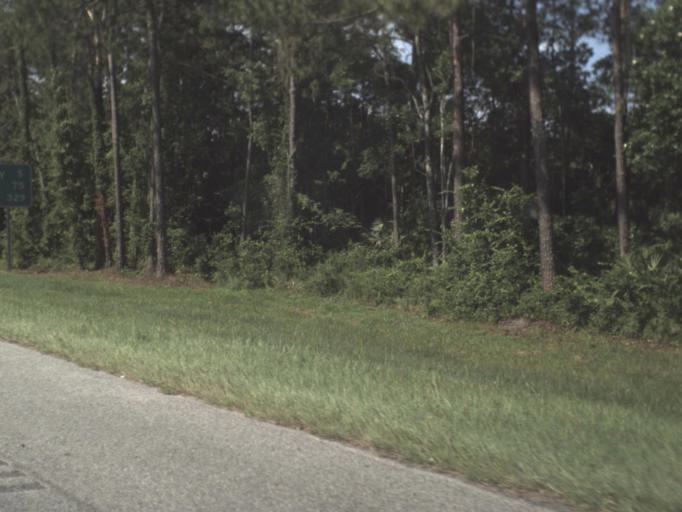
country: US
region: Florida
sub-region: Saint Johns County
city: Fruit Cove
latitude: 30.0509
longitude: -81.4974
